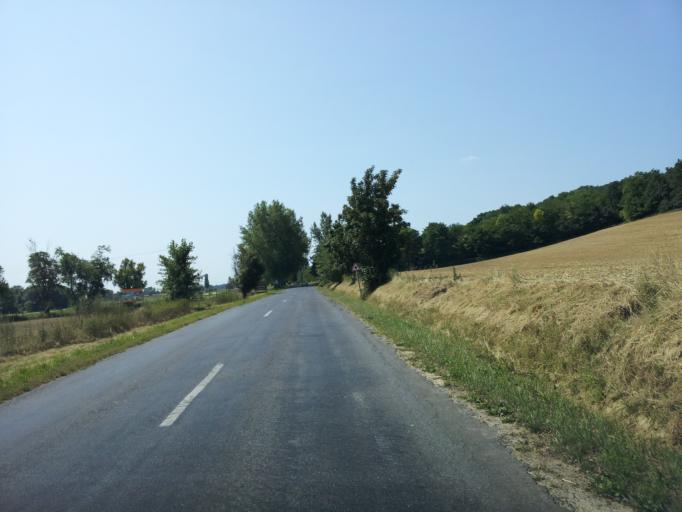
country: HU
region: Zala
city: Heviz
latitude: 46.8301
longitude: 17.0926
